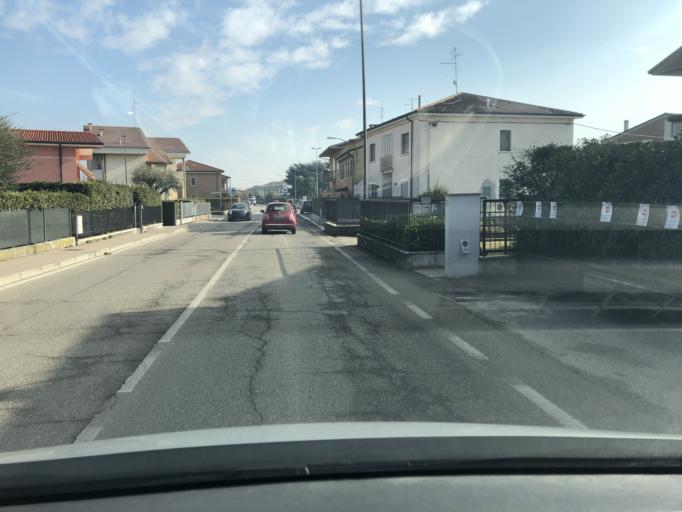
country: IT
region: Veneto
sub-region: Provincia di Verona
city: Lugagnano
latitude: 45.4324
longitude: 10.8783
